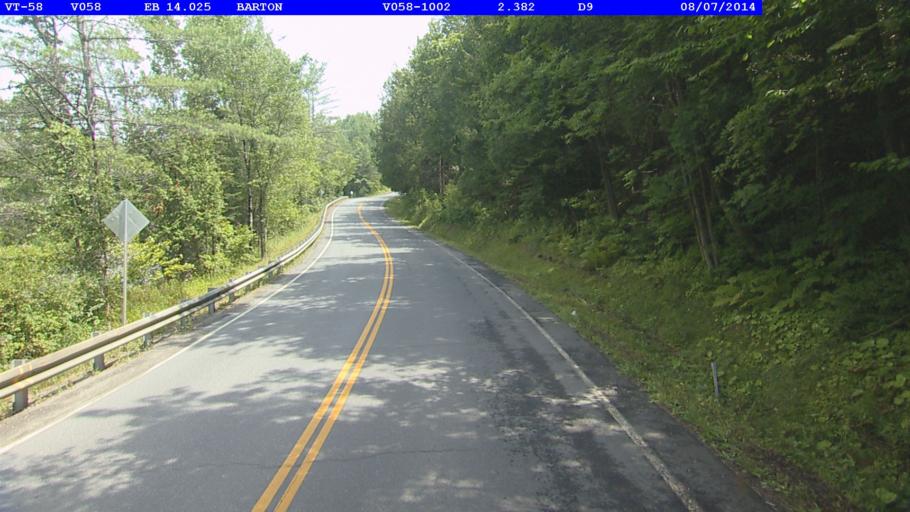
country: US
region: Vermont
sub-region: Orleans County
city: Newport
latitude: 44.8056
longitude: -72.1705
